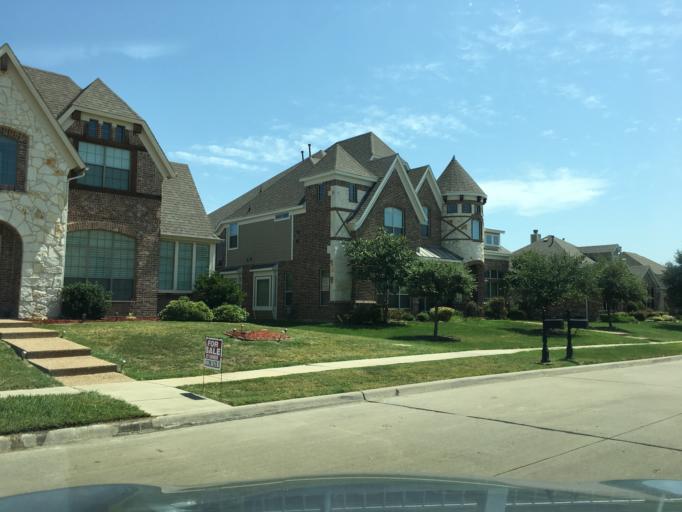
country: US
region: Texas
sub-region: Dallas County
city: Rowlett
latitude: 32.8879
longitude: -96.6014
